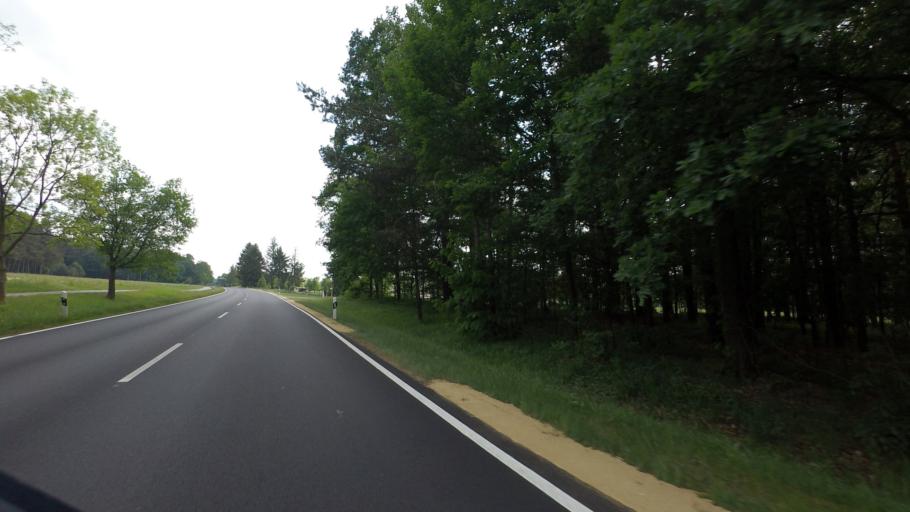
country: DE
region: Saxony
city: Rietschen
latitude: 51.3674
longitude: 14.7968
